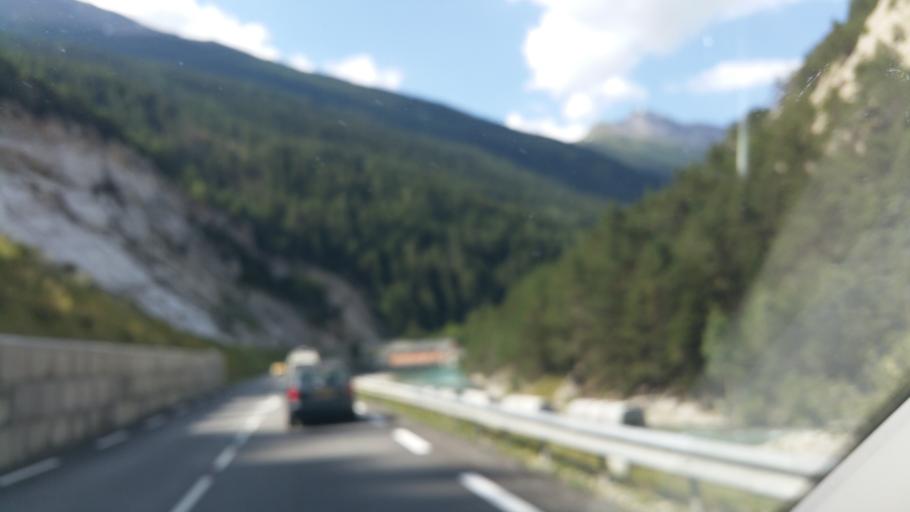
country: FR
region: Rhone-Alpes
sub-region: Departement de la Savoie
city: Modane
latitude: 45.2227
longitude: 6.7622
